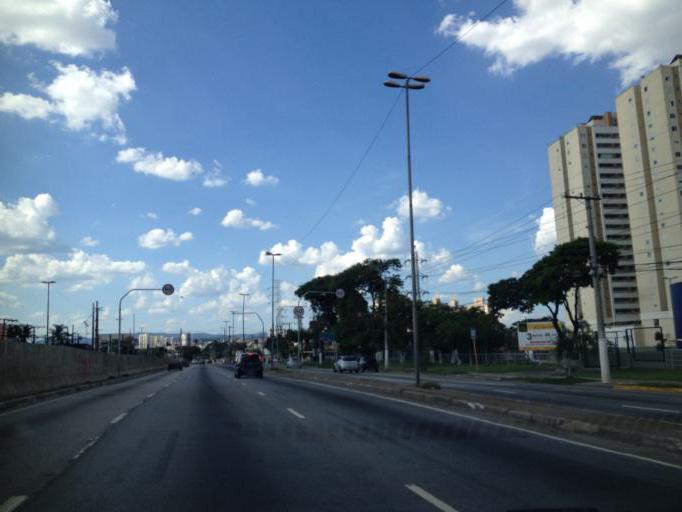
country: BR
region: Sao Paulo
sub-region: Sao Paulo
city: Sao Paulo
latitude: -23.5368
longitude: -46.5824
